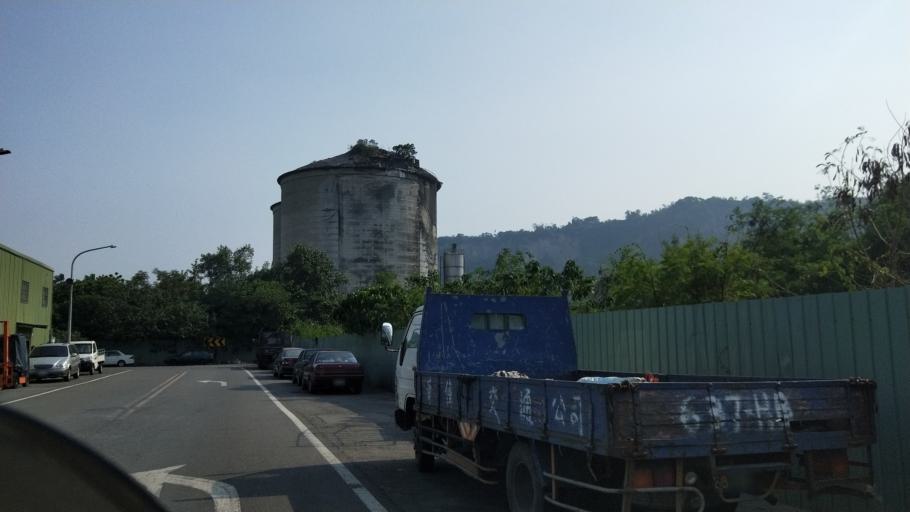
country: TW
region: Kaohsiung
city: Kaohsiung
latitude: 22.6472
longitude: 120.2756
